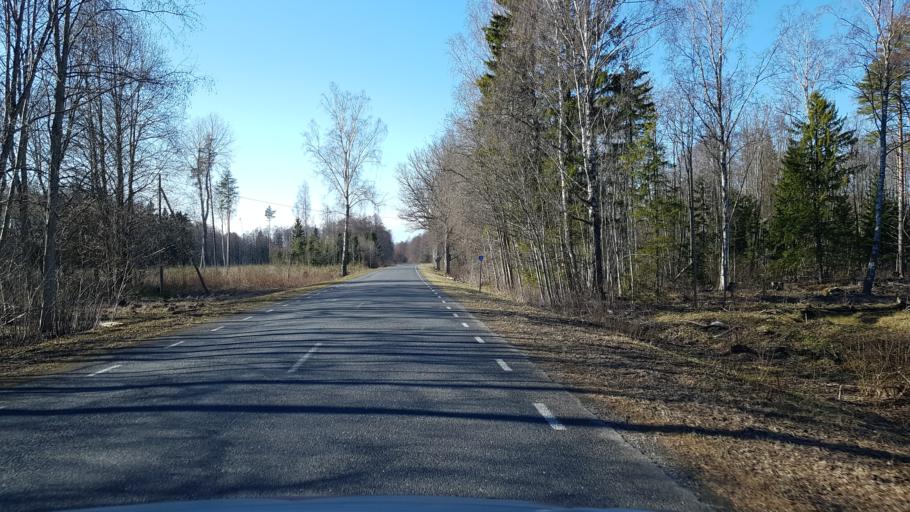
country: EE
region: Laeaene-Virumaa
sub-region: Kadrina vald
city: Kadrina
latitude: 59.5224
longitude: 26.0828
